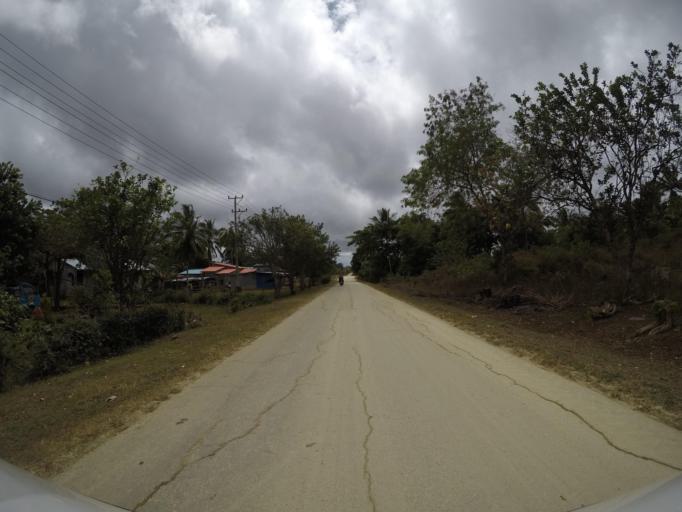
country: TL
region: Lautem
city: Lospalos
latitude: -8.4665
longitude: 126.9948
